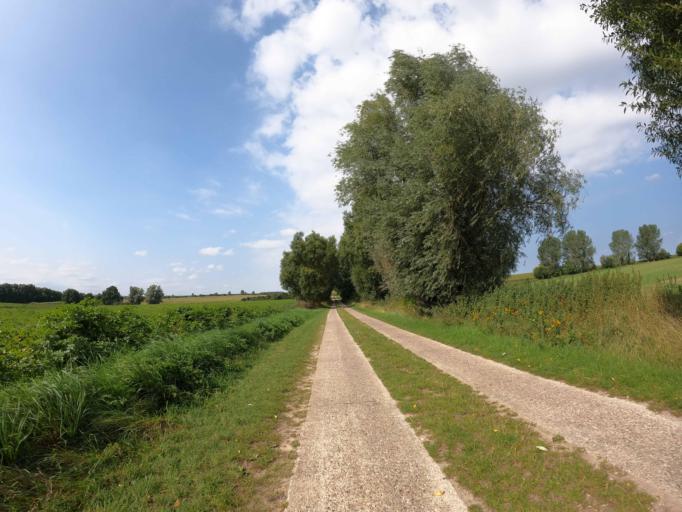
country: DE
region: Mecklenburg-Vorpommern
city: Malchow
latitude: 53.4395
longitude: 12.4821
